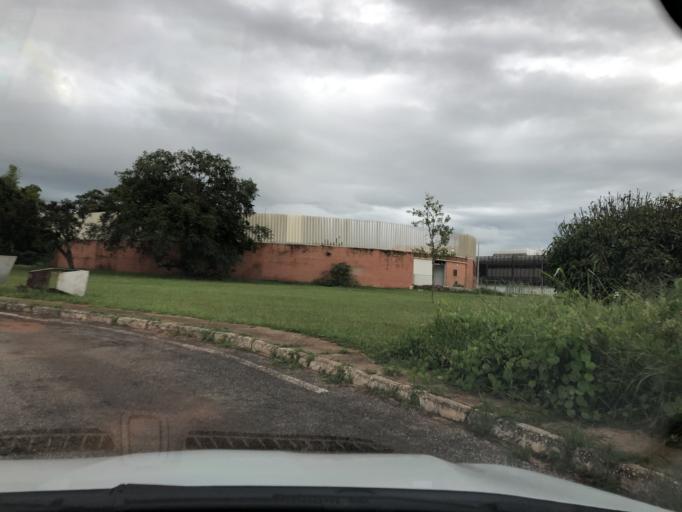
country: BR
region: Federal District
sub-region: Brasilia
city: Brasilia
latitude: -15.7728
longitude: -47.8701
